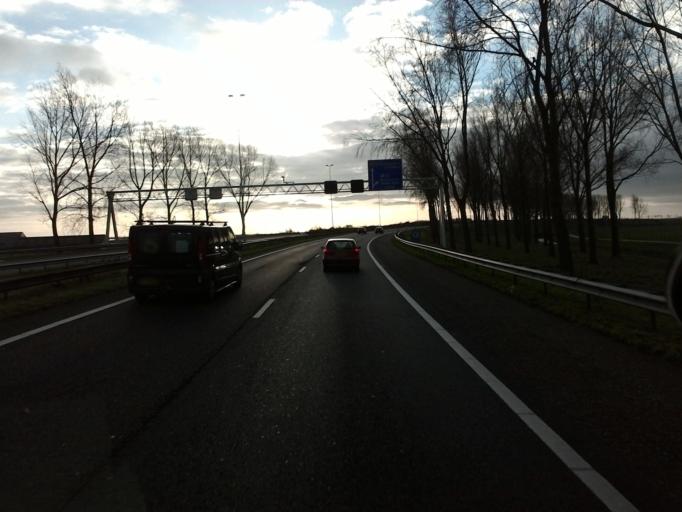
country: NL
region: South Holland
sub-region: Gemeente Waddinxveen
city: Waddinxveen
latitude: 52.0147
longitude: 4.6543
